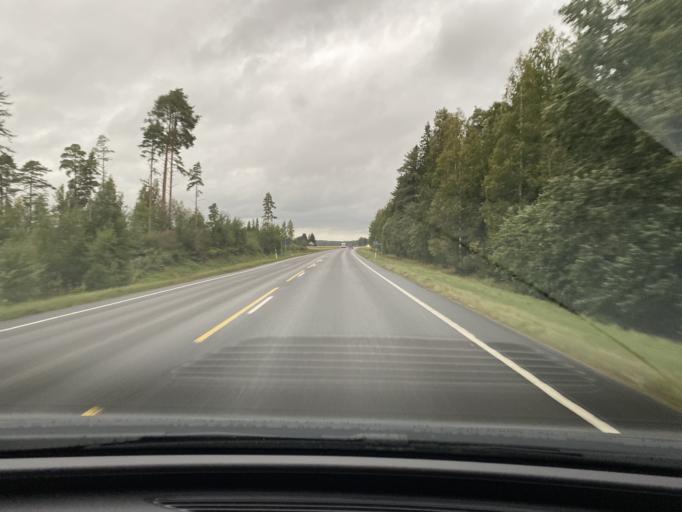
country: FI
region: Satakunta
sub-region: Pori
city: Vampula
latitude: 61.0199
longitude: 22.6634
